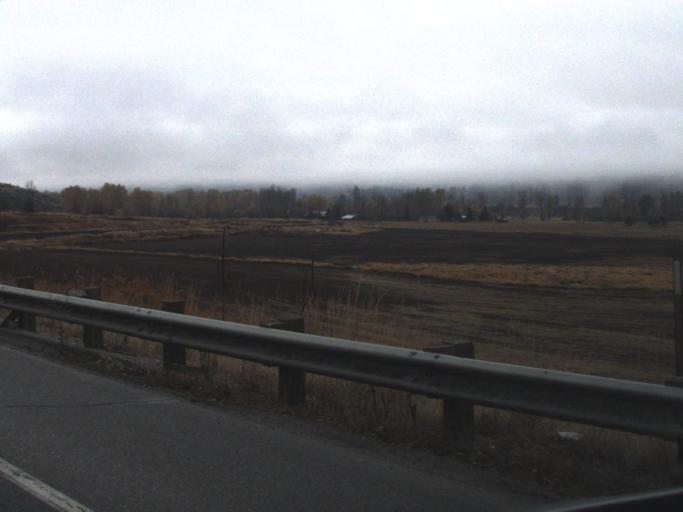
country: US
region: Washington
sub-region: Stevens County
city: Kettle Falls
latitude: 48.5977
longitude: -118.0084
